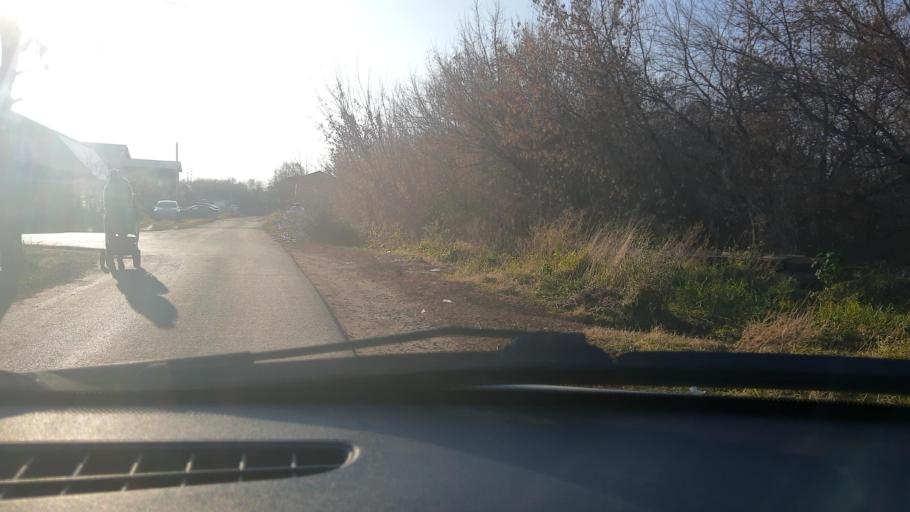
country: RU
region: Bashkortostan
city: Avdon
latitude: 54.6999
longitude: 55.8165
